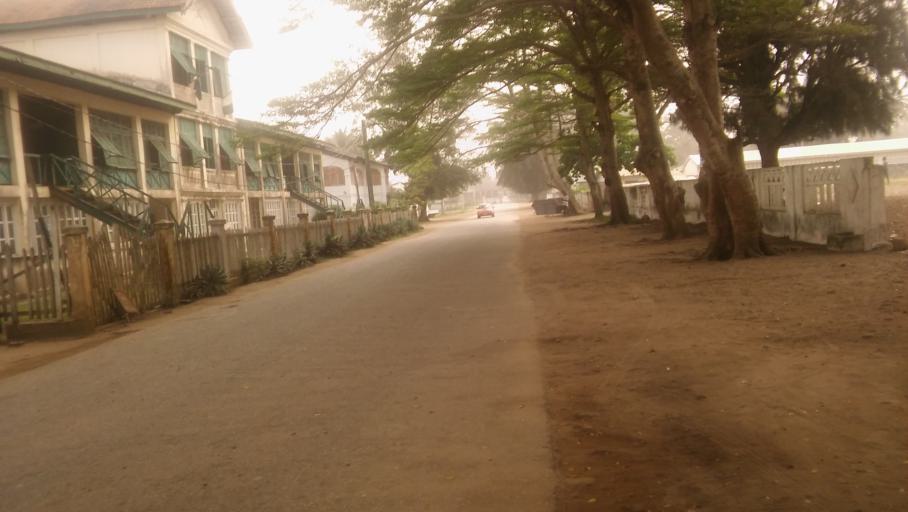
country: CI
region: Sud-Comoe
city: Grand-Bassam
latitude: 5.1951
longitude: -3.7347
